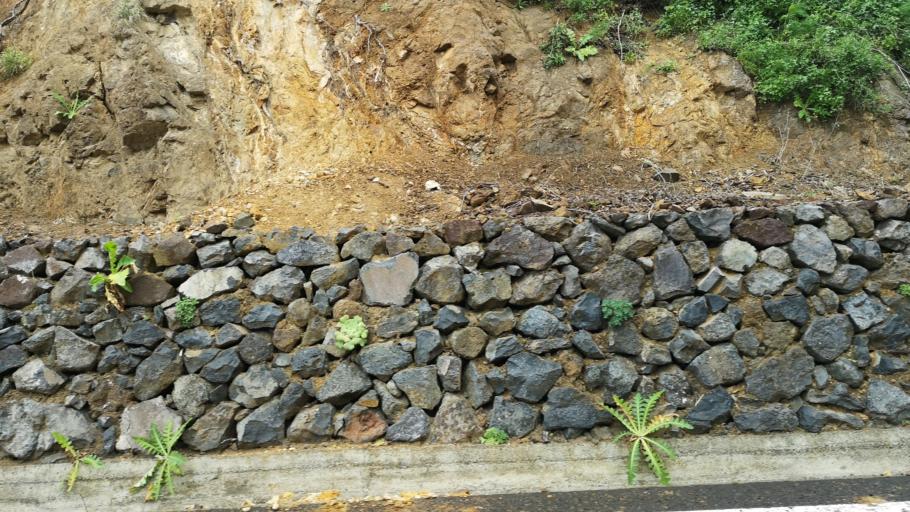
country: ES
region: Canary Islands
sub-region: Provincia de Santa Cruz de Tenerife
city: Hermigua
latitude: 28.1431
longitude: -17.1991
